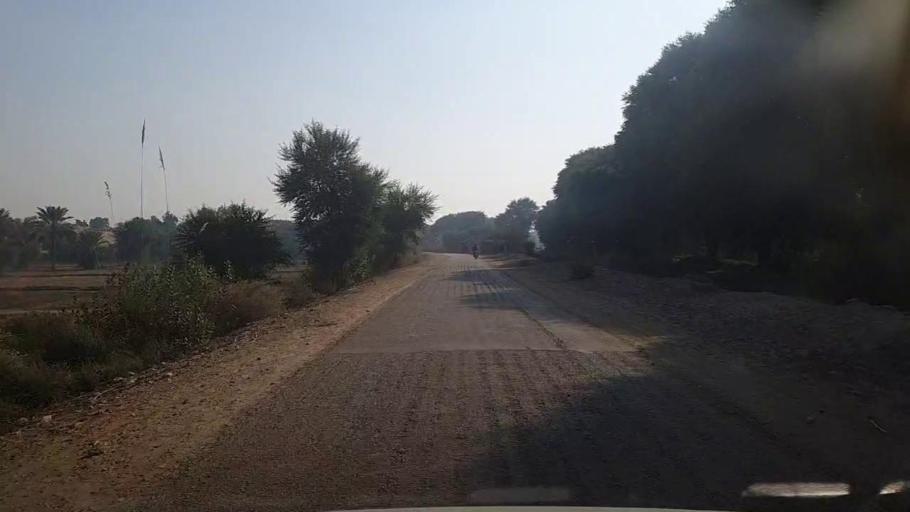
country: PK
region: Sindh
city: Kandiari
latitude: 26.8390
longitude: 68.4891
